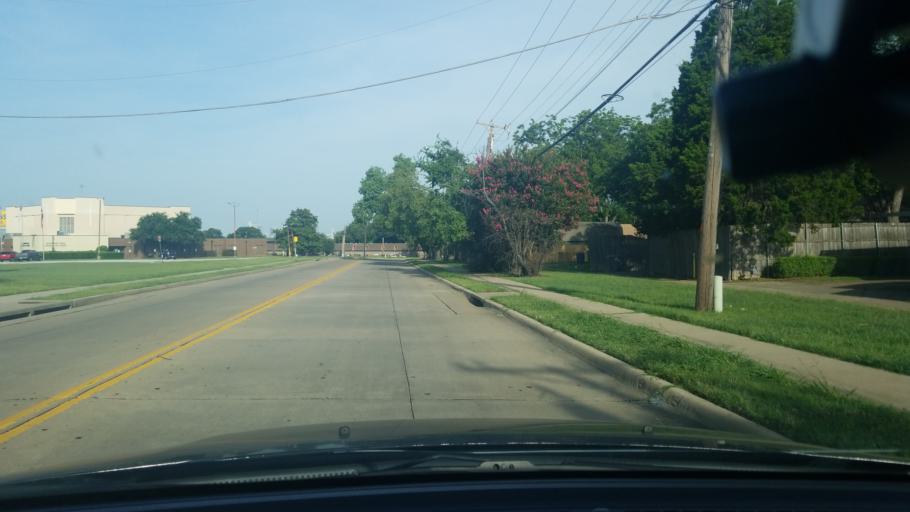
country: US
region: Texas
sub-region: Dallas County
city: Highland Park
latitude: 32.7955
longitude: -96.7049
